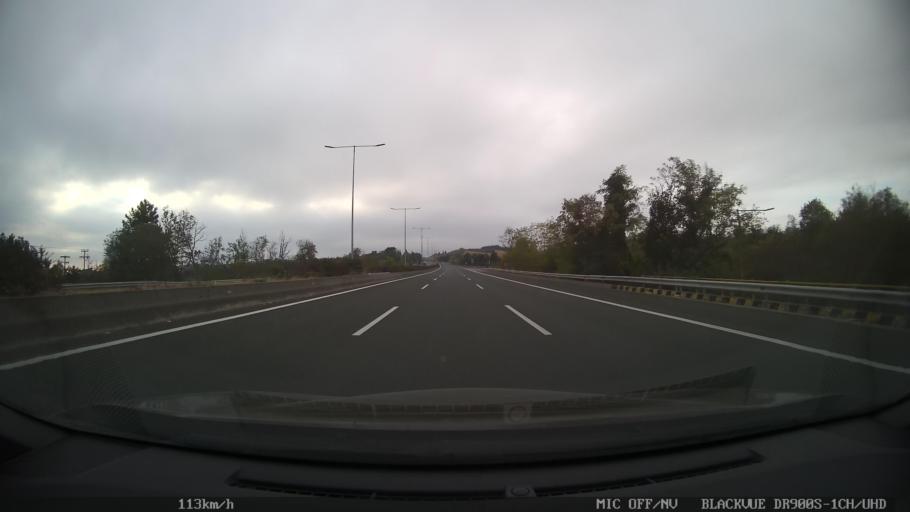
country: GR
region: Central Macedonia
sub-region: Nomos Pierias
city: Makrygialos
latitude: 40.4597
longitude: 22.5784
